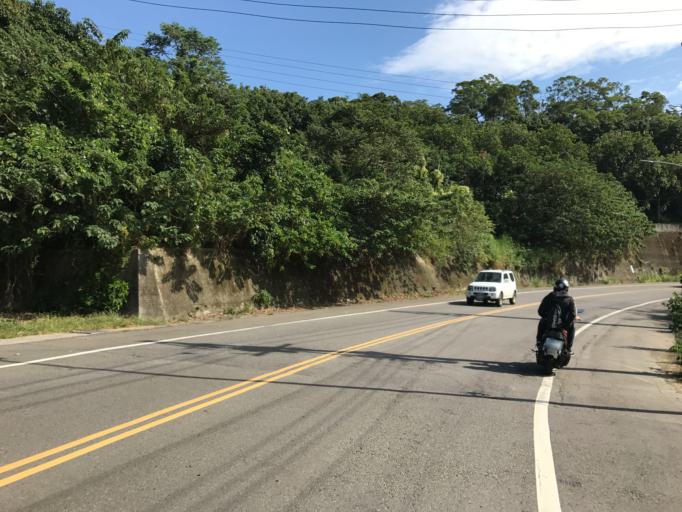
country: TW
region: Taiwan
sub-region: Hsinchu
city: Hsinchu
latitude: 24.7692
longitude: 120.9910
